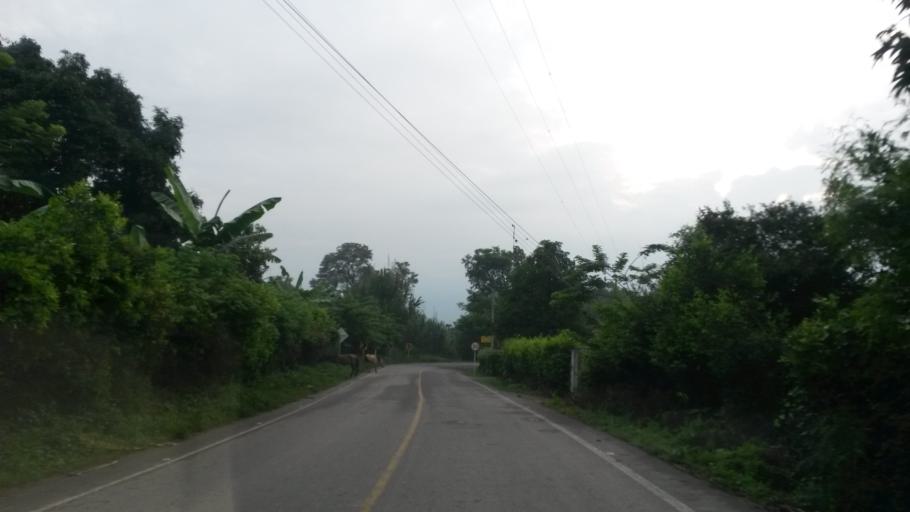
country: CO
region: Cauca
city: Padilla
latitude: 3.2281
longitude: -76.3200
